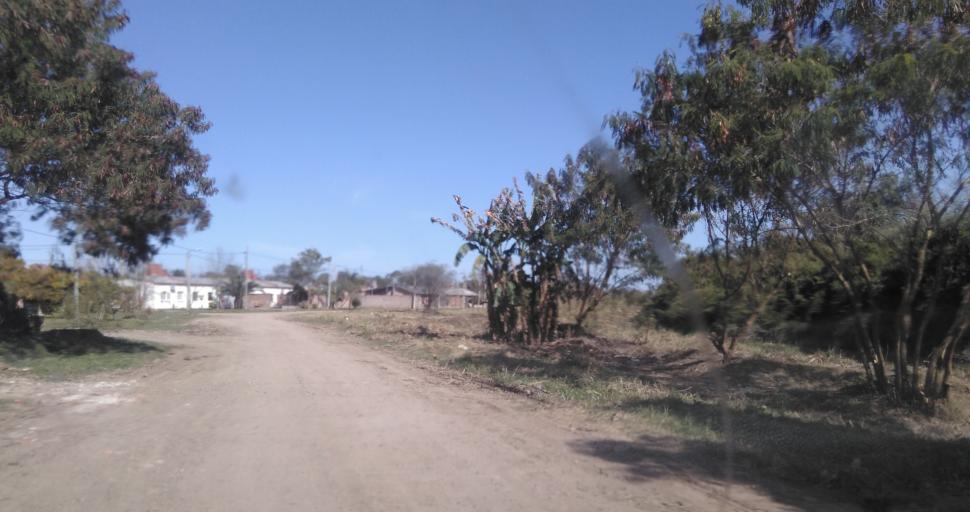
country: AR
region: Chaco
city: Fontana
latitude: -27.4368
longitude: -59.0253
